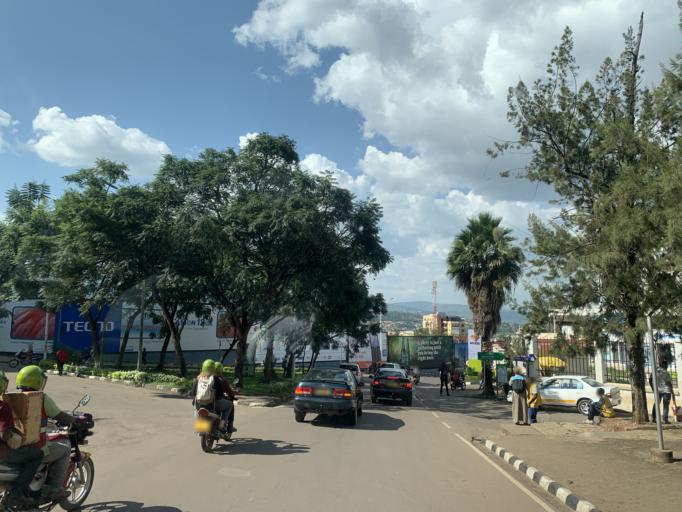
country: RW
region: Kigali
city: Kigali
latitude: -1.9460
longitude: 30.0607
